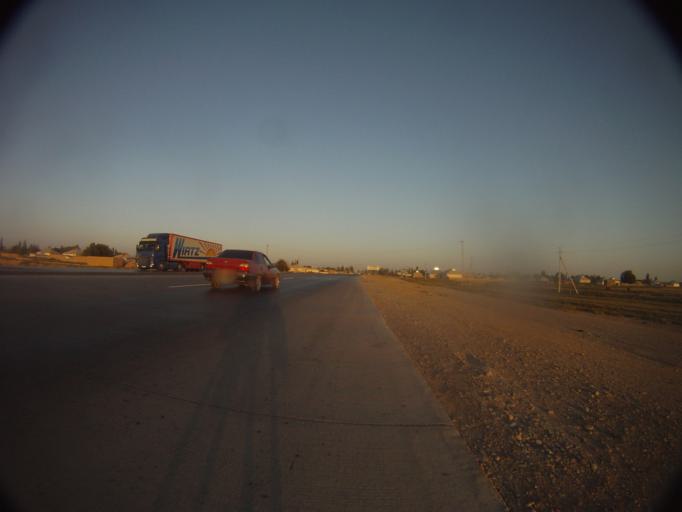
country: KZ
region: Ongtustik Qazaqstan
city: Turkestan
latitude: 43.2645
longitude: 68.3662
